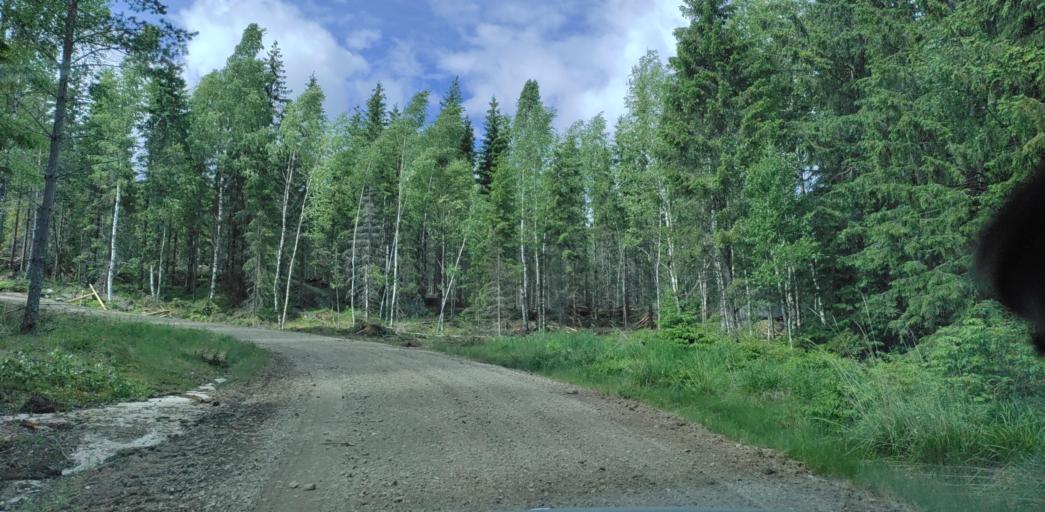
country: SE
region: Vaermland
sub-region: Munkfors Kommun
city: Munkfors
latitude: 59.9701
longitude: 13.4022
